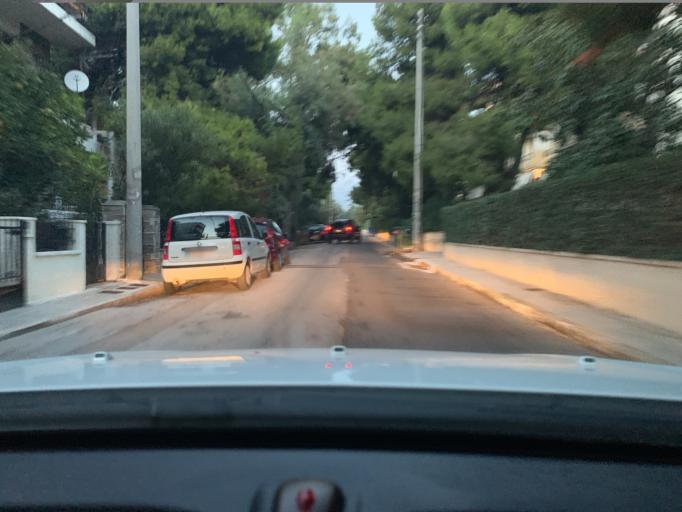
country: GR
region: Attica
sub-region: Nomarchia Athinas
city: Vrilissia
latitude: 38.0314
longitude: 23.8314
